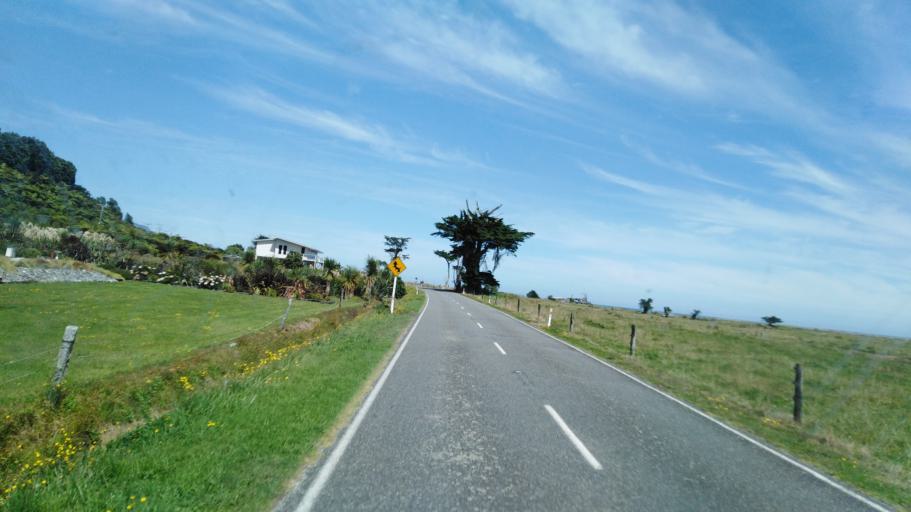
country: NZ
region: West Coast
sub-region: Buller District
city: Westport
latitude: -41.5363
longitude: 171.9318
